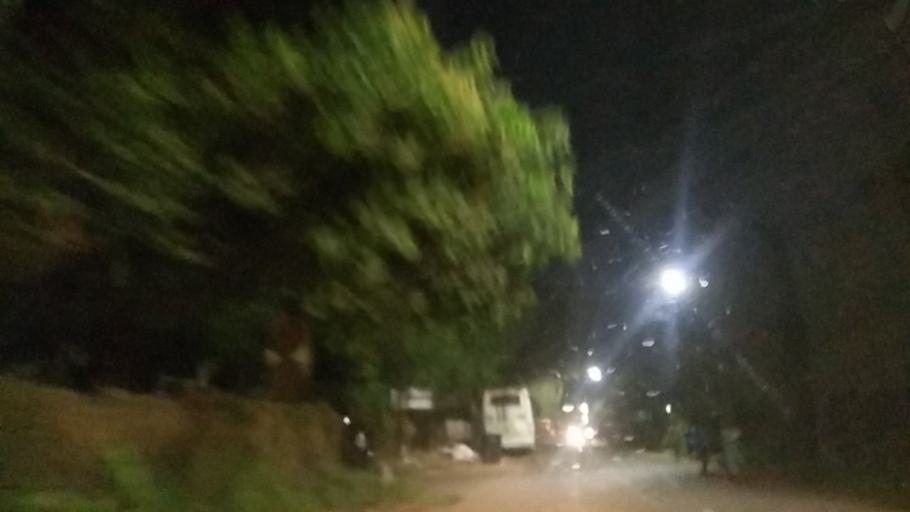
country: IN
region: Goa
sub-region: South Goa
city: Raia
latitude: 15.2988
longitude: 73.9694
